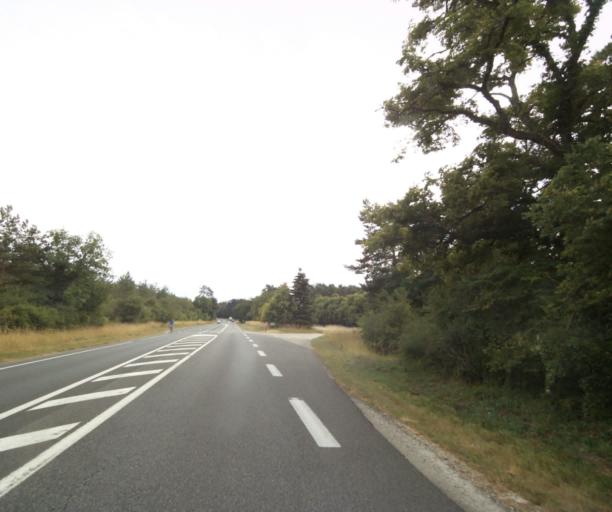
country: FR
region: Ile-de-France
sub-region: Departement de Seine-et-Marne
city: Bois-le-Roi
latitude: 48.4418
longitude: 2.6897
